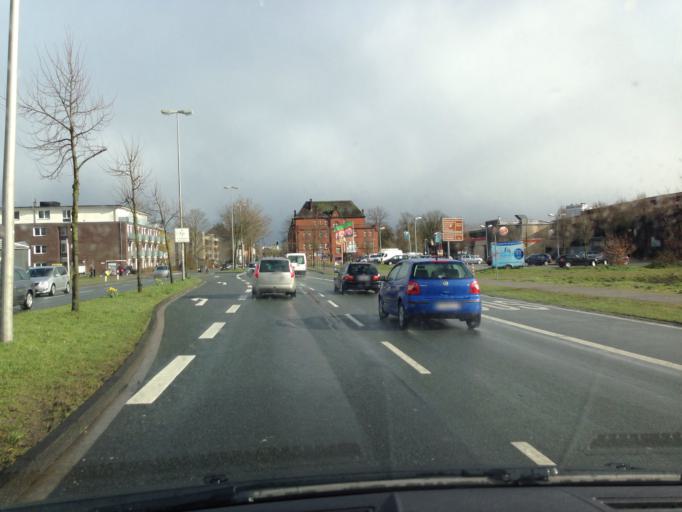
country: DE
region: North Rhine-Westphalia
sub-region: Regierungsbezirk Munster
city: Muenster
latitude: 51.9777
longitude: 7.5993
